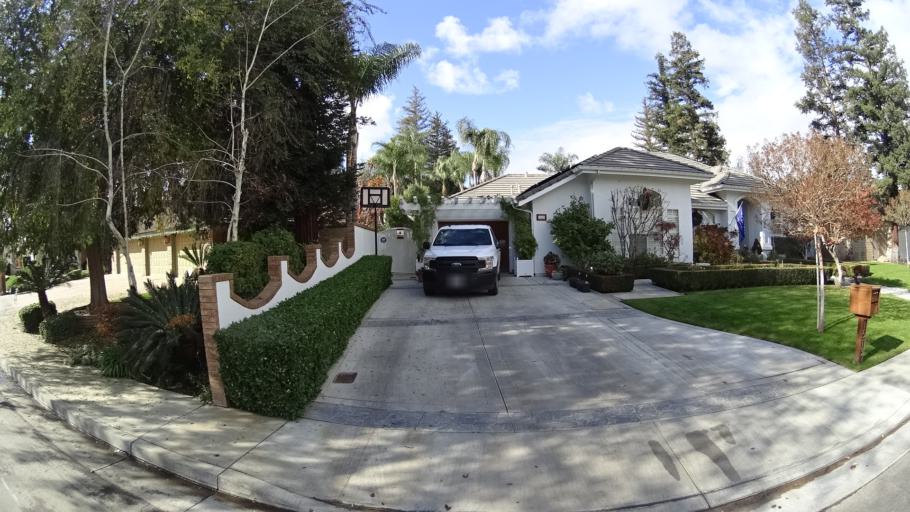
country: US
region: California
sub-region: Kern County
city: Greenacres
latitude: 35.3405
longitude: -119.0868
